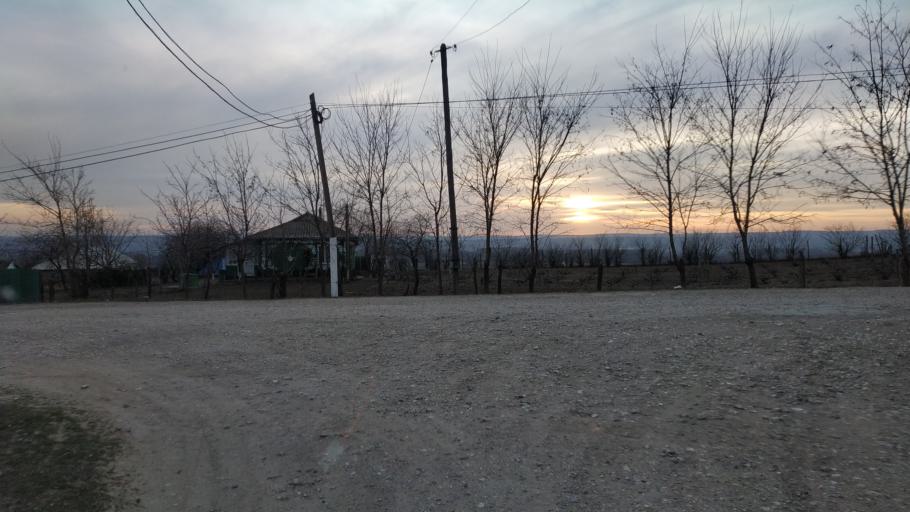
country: MD
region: Hincesti
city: Dancu
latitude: 46.7469
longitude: 28.2092
